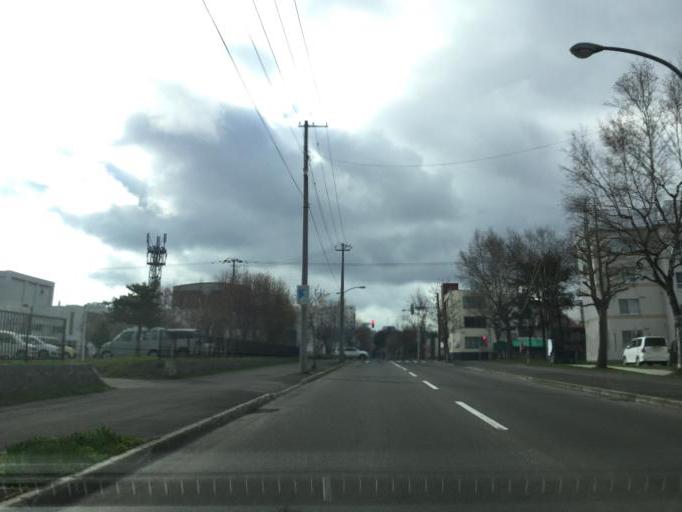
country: JP
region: Hokkaido
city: Ebetsu
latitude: 43.0760
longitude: 141.4913
